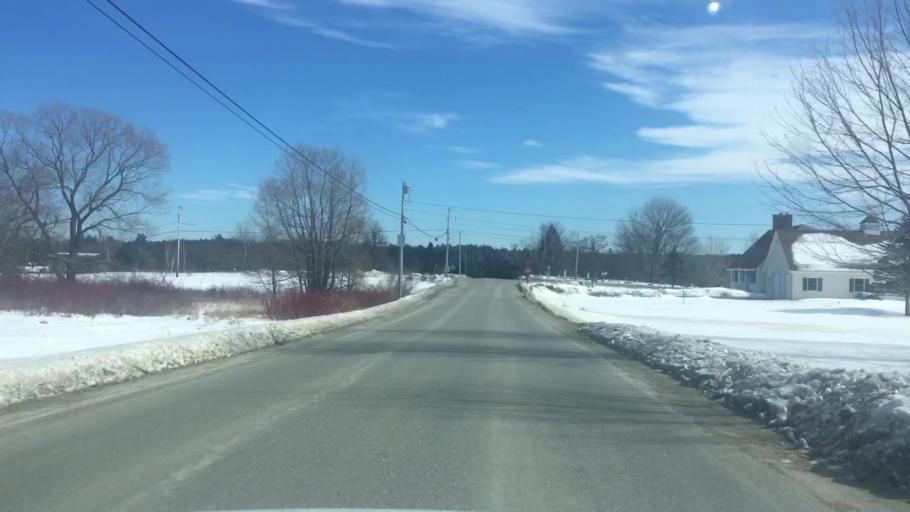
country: US
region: Maine
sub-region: Penobscot County
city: Eddington
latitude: 44.7981
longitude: -68.6735
